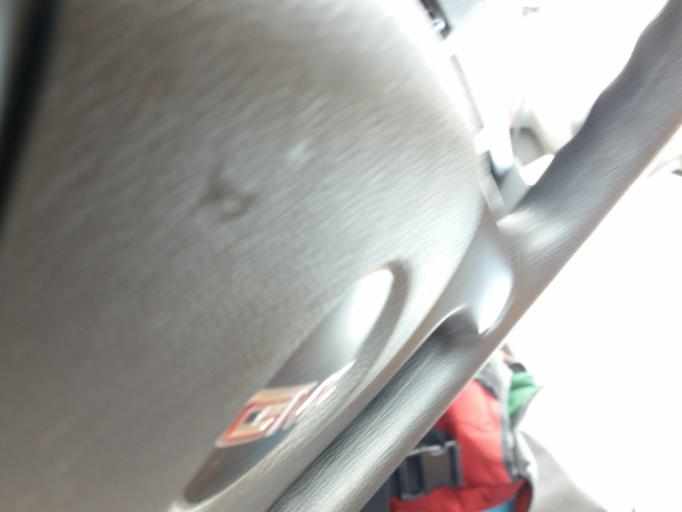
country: US
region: Illinois
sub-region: McLean County
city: Hudson
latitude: 40.5847
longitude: -89.0027
